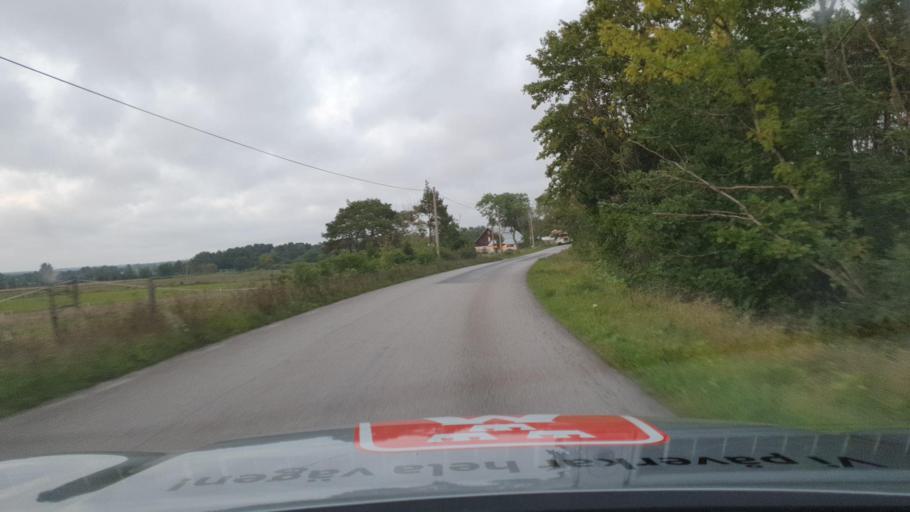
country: SE
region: Gotland
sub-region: Gotland
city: Klintehamn
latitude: 57.2818
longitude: 18.2592
